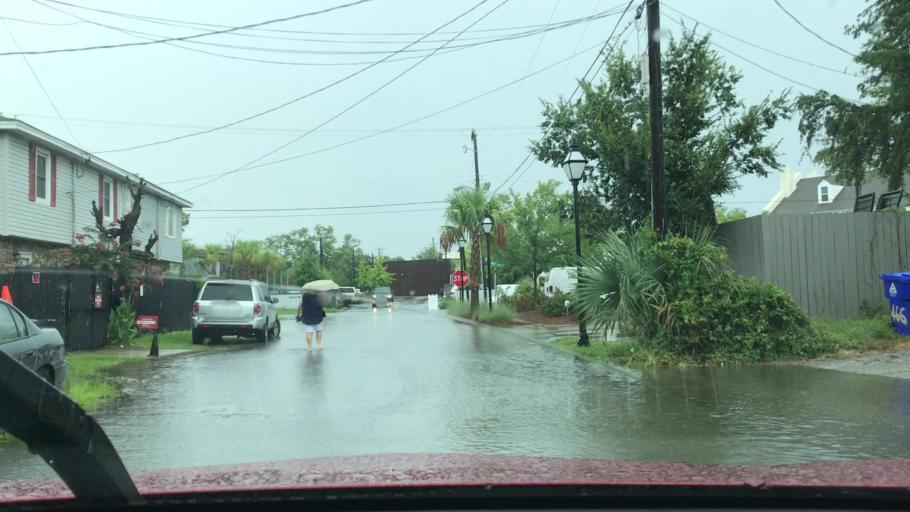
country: US
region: South Carolina
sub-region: Charleston County
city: Charleston
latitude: 32.8087
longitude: -79.9468
